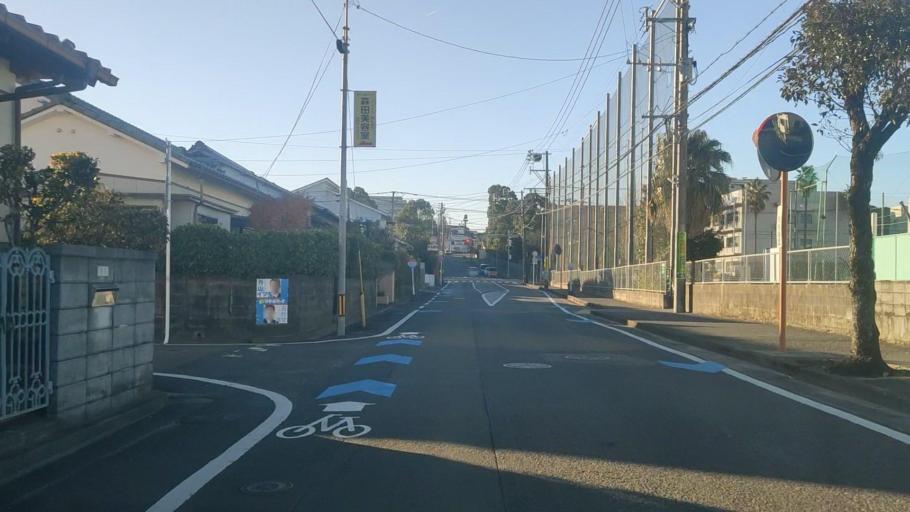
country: JP
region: Miyazaki
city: Miyazaki-shi
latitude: 31.9003
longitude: 131.4145
